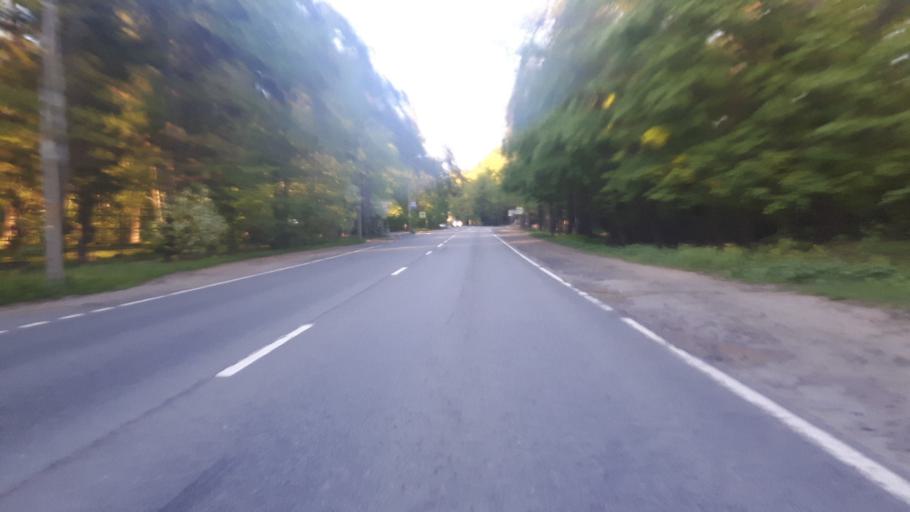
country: RU
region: St.-Petersburg
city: Zelenogorsk
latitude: 60.1932
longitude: 29.6620
